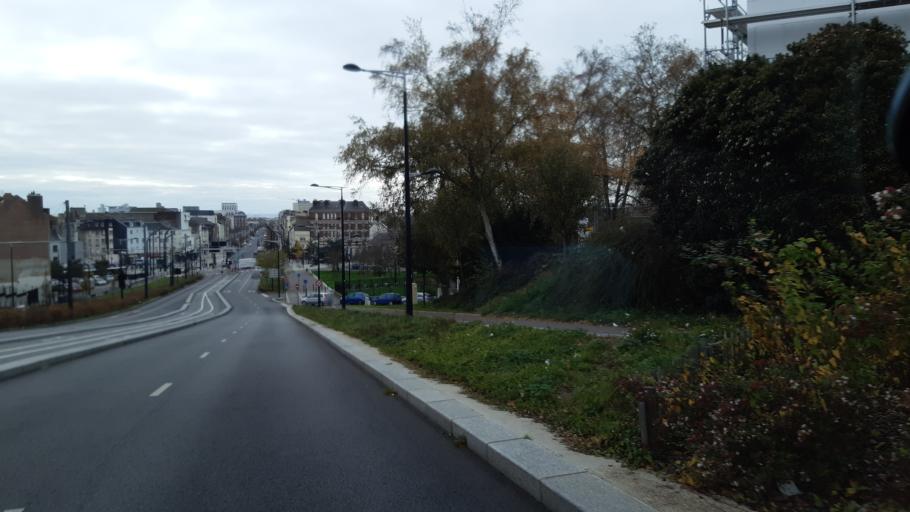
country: FR
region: Haute-Normandie
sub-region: Departement de la Seine-Maritime
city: Le Havre
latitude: 49.5018
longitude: 0.1311
